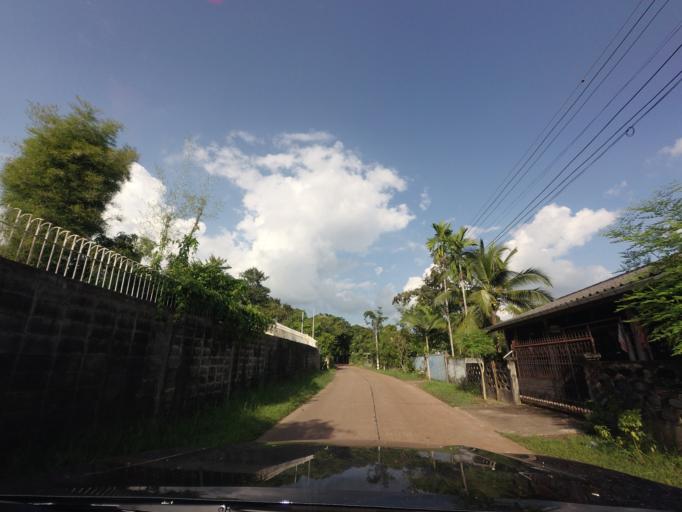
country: TH
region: Nong Khai
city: Nong Khai
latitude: 17.8867
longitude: 102.7765
